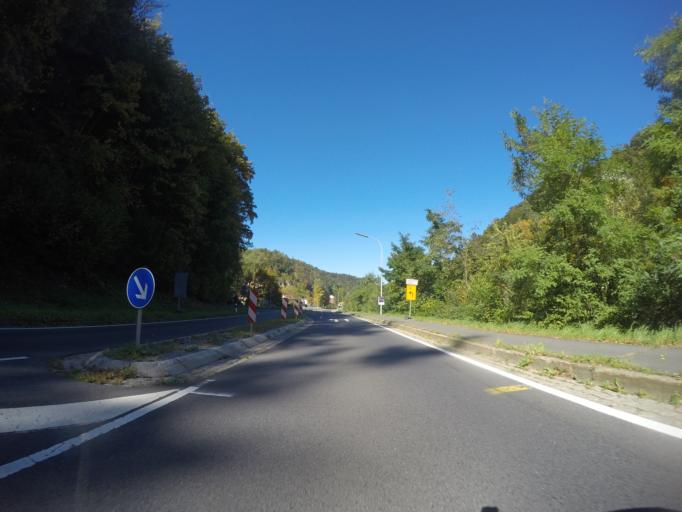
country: DE
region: Bavaria
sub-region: Upper Franconia
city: Gossweinstein
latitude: 49.7771
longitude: 11.3356
